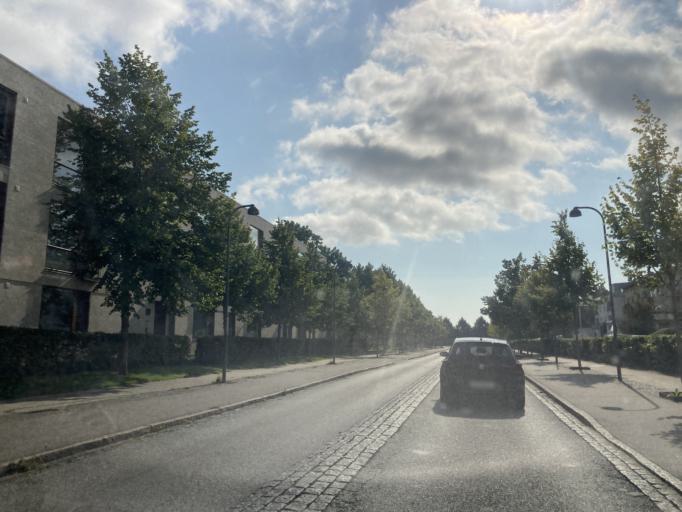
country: DK
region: Capital Region
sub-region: Horsholm Kommune
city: Horsholm
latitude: 55.8804
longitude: 12.4989
